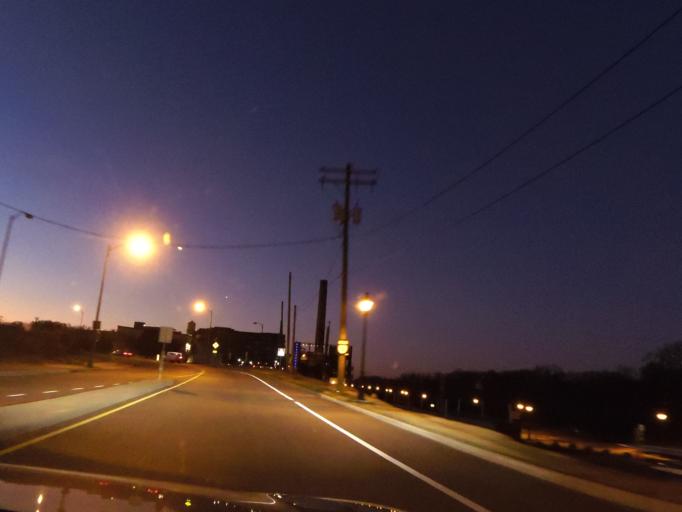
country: US
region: Virginia
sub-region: Henrico County
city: Montrose
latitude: 37.5200
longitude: -77.4158
